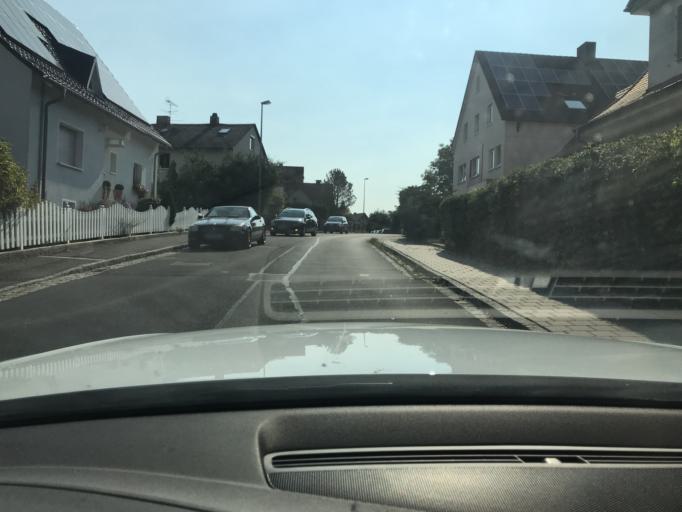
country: DE
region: Bavaria
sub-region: Upper Franconia
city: Pegnitz
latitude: 49.7544
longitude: 11.5475
